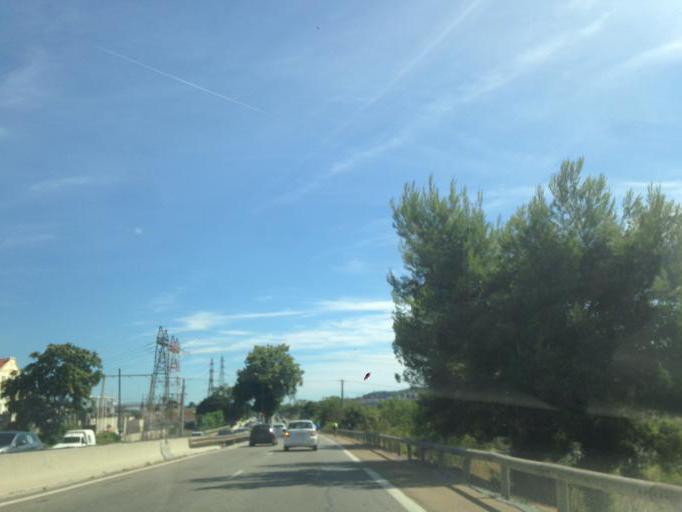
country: FR
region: Provence-Alpes-Cote d'Azur
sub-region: Departement des Alpes-Maritimes
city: La Gaude
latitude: 43.7212
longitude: 7.1862
